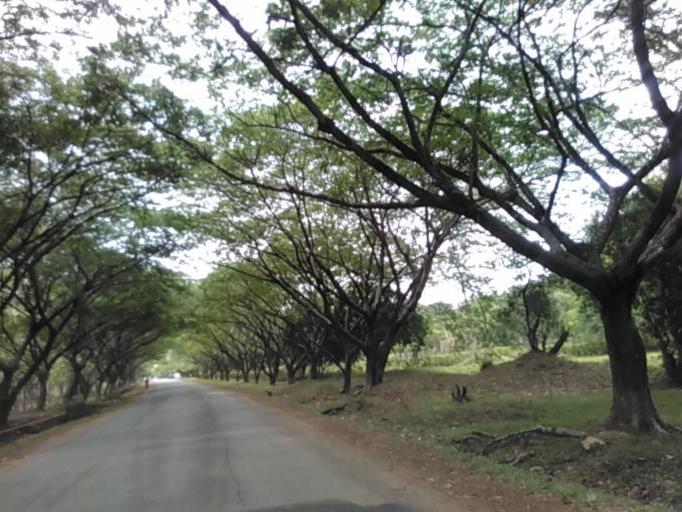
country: GH
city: Akropong
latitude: 6.0950
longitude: 0.1116
